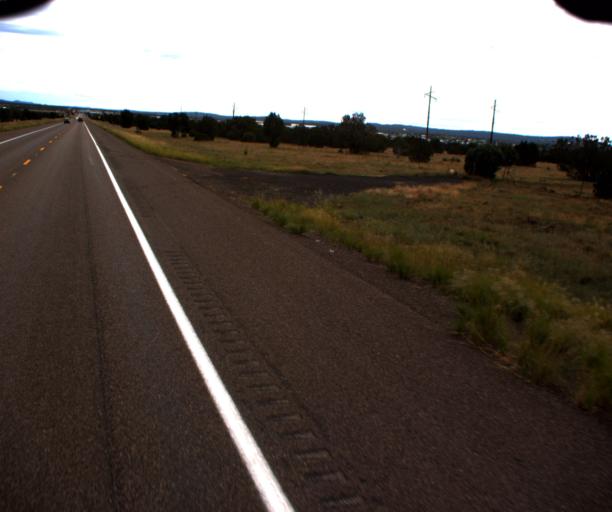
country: US
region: Arizona
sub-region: Navajo County
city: Show Low
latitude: 34.2794
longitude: -110.0268
